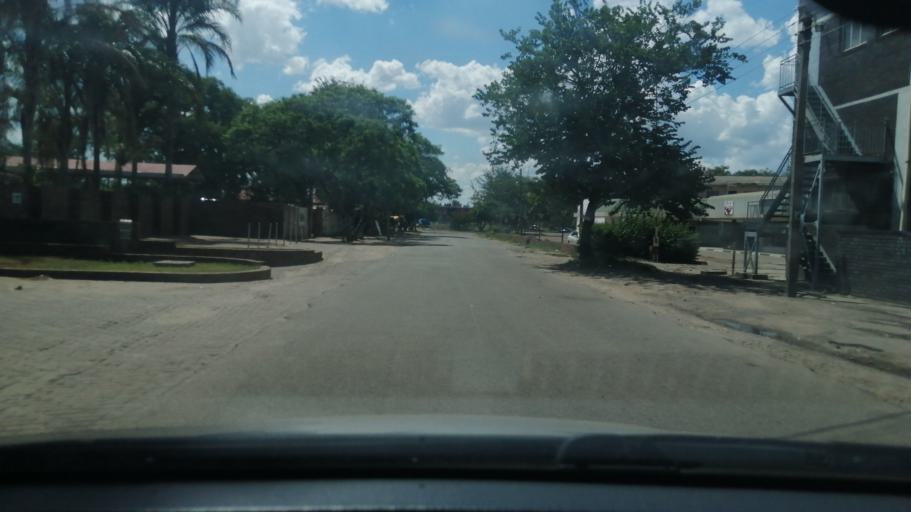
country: ZW
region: Harare
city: Harare
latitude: -17.8109
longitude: 31.0753
